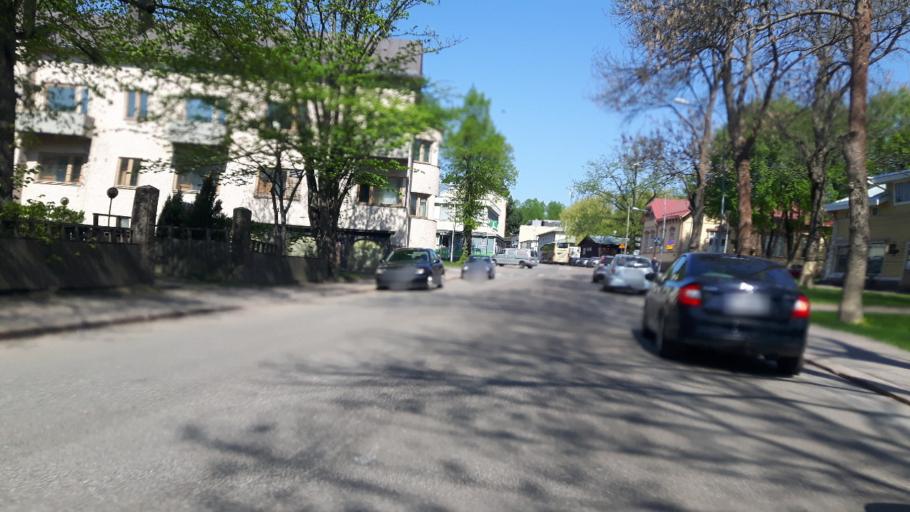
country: FI
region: Uusimaa
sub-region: Loviisa
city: Lovisa
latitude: 60.4552
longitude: 26.2302
